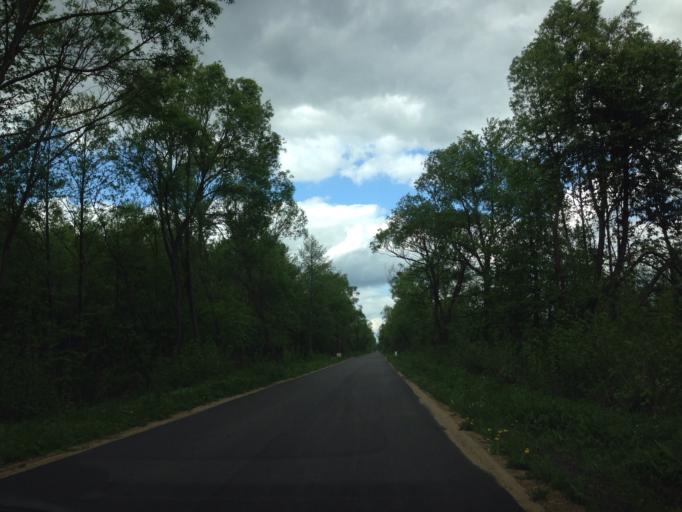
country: PL
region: Podlasie
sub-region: Powiat bialostocki
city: Tykocin
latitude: 53.3008
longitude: 22.6047
